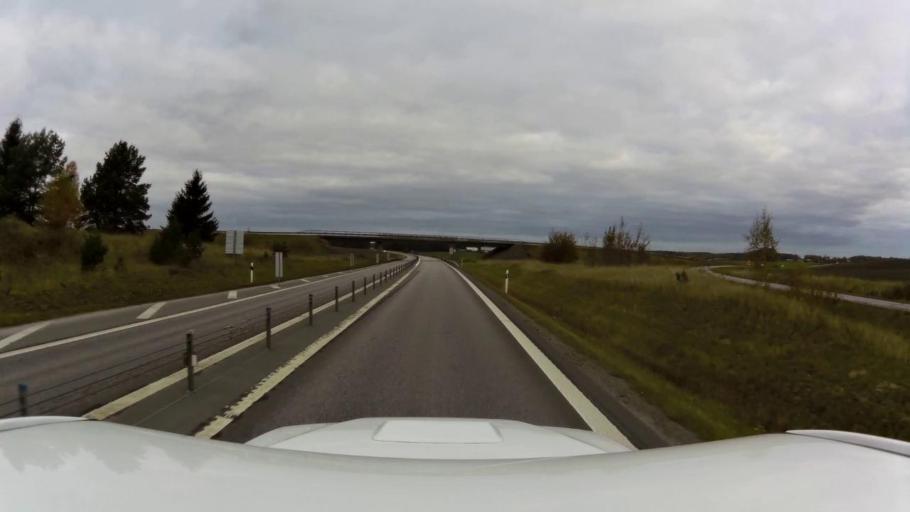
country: SE
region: OEstergoetland
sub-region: Linkopings Kommun
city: Ljungsbro
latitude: 58.4784
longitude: 15.4871
